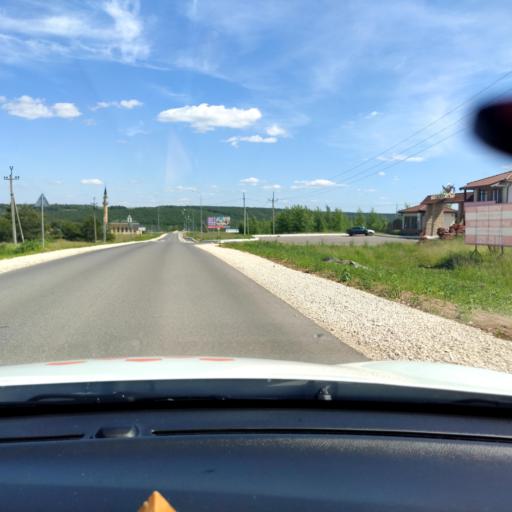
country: RU
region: Tatarstan
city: Osinovo
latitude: 55.7747
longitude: 48.8315
